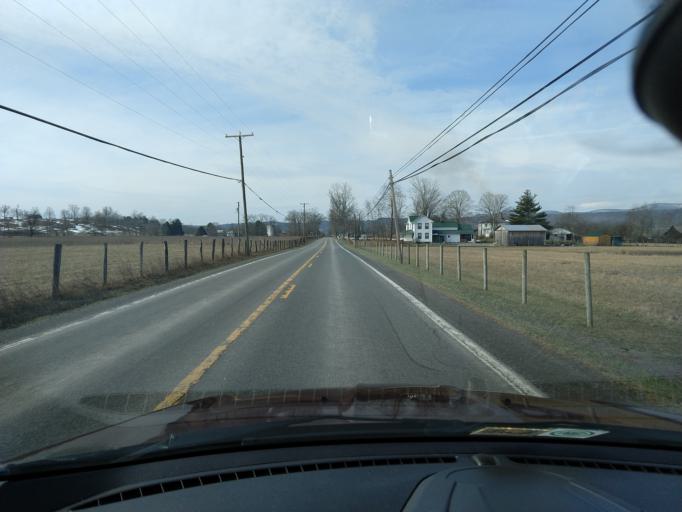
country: US
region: West Virginia
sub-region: Pocahontas County
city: Marlinton
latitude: 38.1424
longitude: -80.2014
